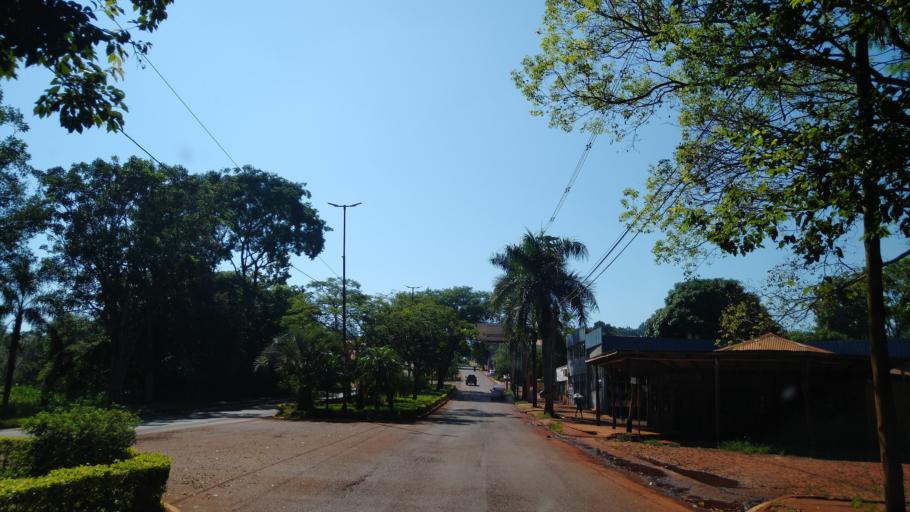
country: AR
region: Misiones
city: Puerto Esperanza
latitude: -26.0227
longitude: -54.6101
